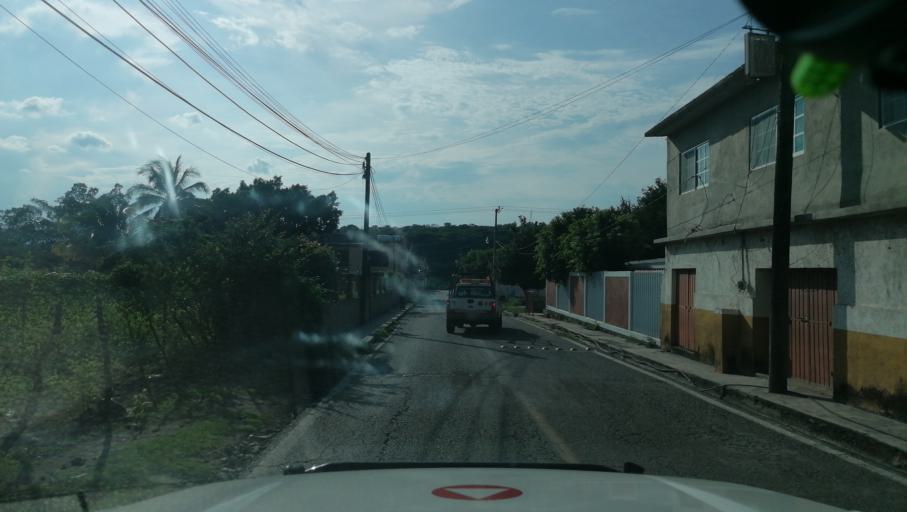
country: MX
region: Morelos
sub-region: Tepalcingo
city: Zacapalco
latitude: 18.6382
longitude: -99.0062
